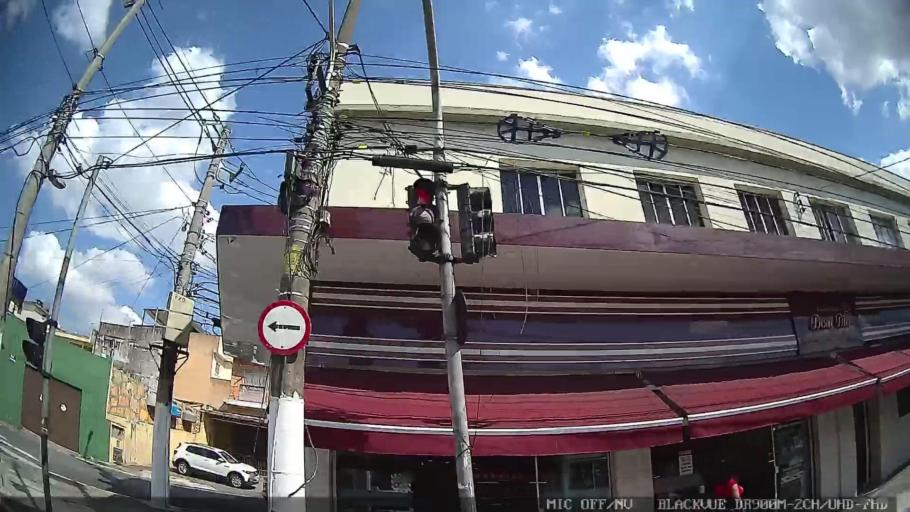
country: BR
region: Sao Paulo
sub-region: Guarulhos
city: Guarulhos
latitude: -23.5064
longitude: -46.4766
